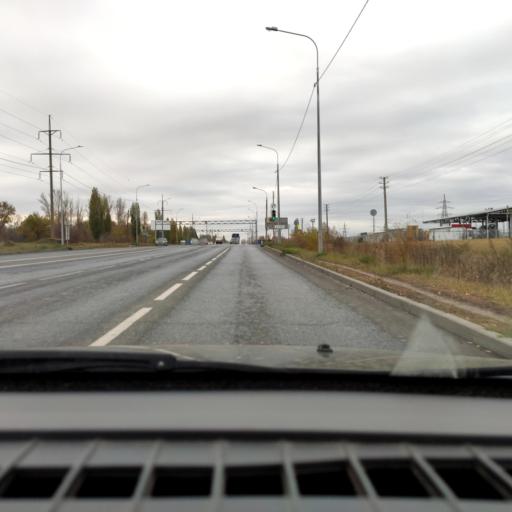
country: RU
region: Samara
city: Tol'yatti
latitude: 53.5657
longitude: 49.2906
